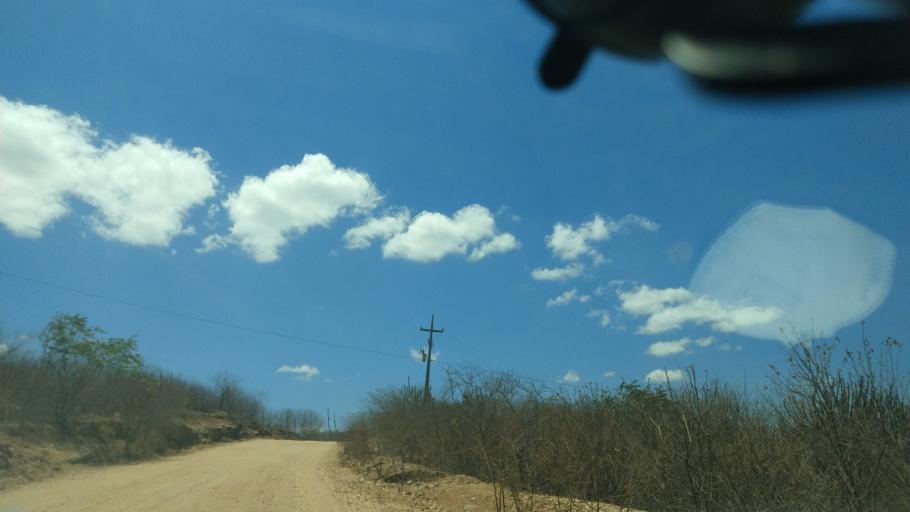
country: BR
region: Rio Grande do Norte
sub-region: Cerro Cora
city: Cerro Cora
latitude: -6.0133
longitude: -36.3028
